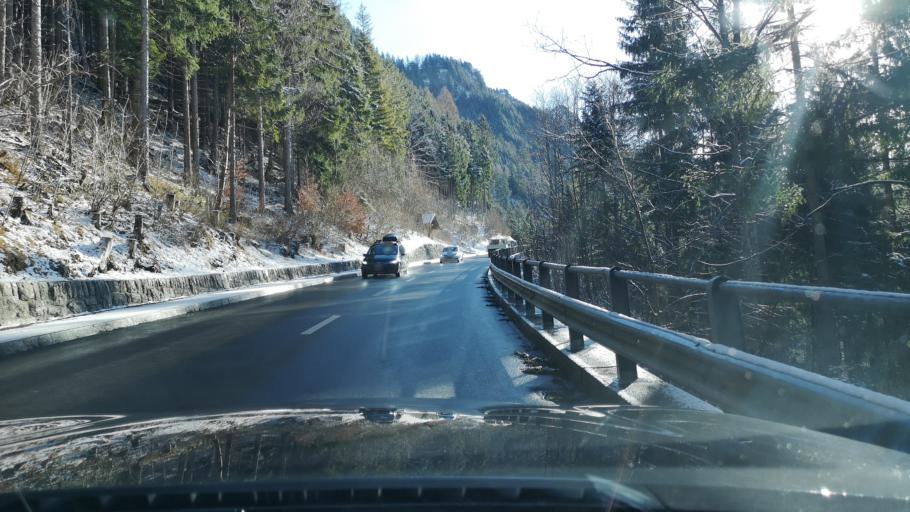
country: LI
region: Triesenberg
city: Triesenberg
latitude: 47.1185
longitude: 9.5580
